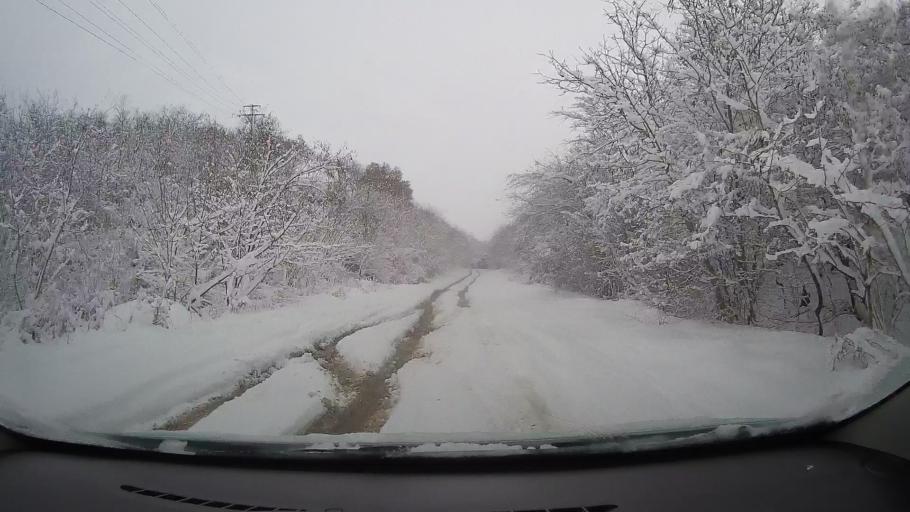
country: RO
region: Alba
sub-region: Comuna Pianu
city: Pianu de Jos
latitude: 45.9626
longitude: 23.4839
